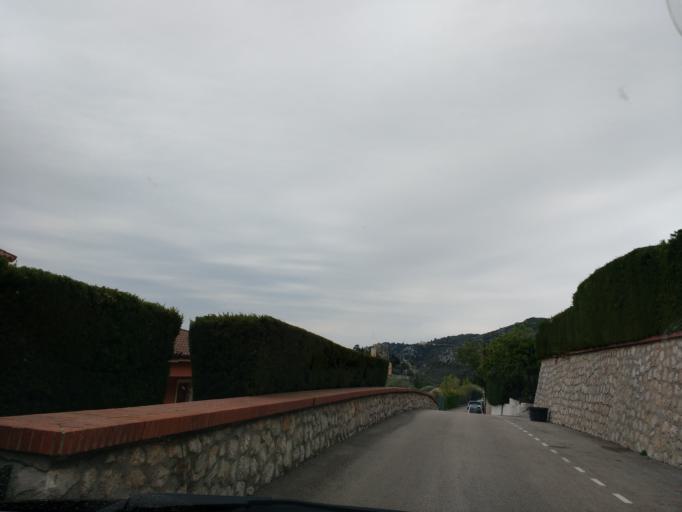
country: FR
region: Provence-Alpes-Cote d'Azur
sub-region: Departement des Alpes-Maritimes
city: Eze
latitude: 43.7302
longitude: 7.3697
